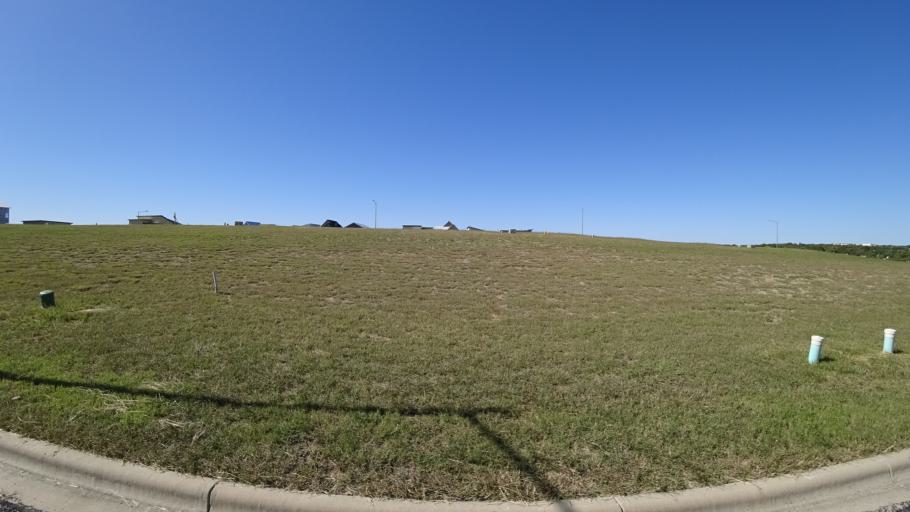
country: US
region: Texas
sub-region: Travis County
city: Hornsby Bend
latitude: 30.2923
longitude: -97.6408
